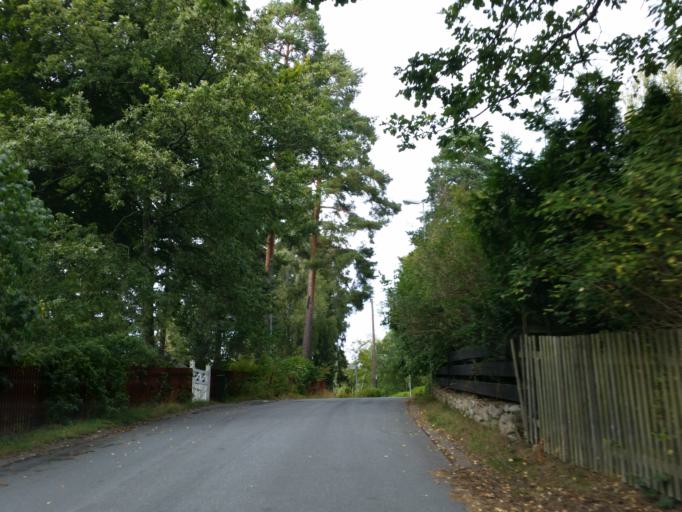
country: SE
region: Stockholm
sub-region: Sollentuna Kommun
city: Sollentuna
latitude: 59.4566
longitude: 17.9301
